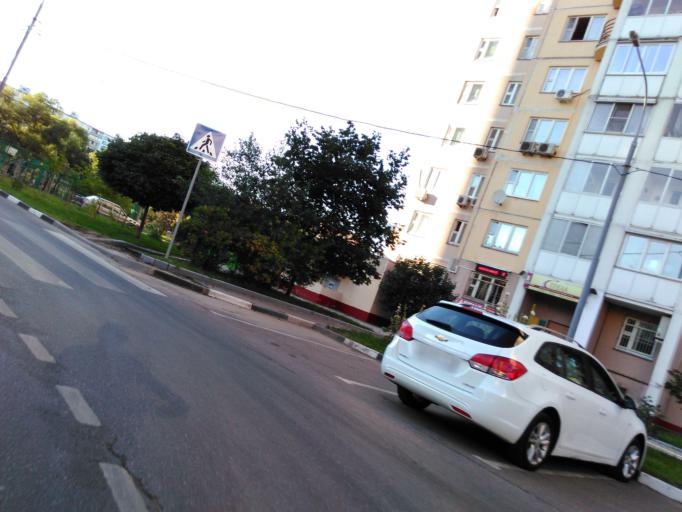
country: RU
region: Moscow
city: Tyoply Stan
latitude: 55.6399
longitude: 37.5131
